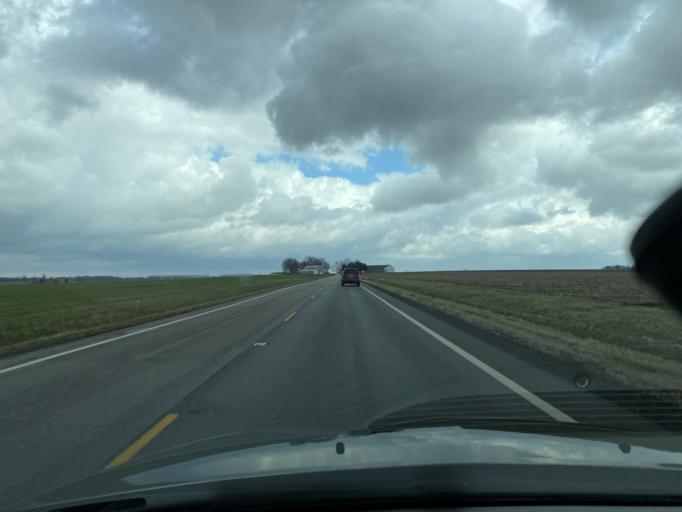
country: US
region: Ohio
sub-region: Wayne County
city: Smithville
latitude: 40.8459
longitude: -81.8835
